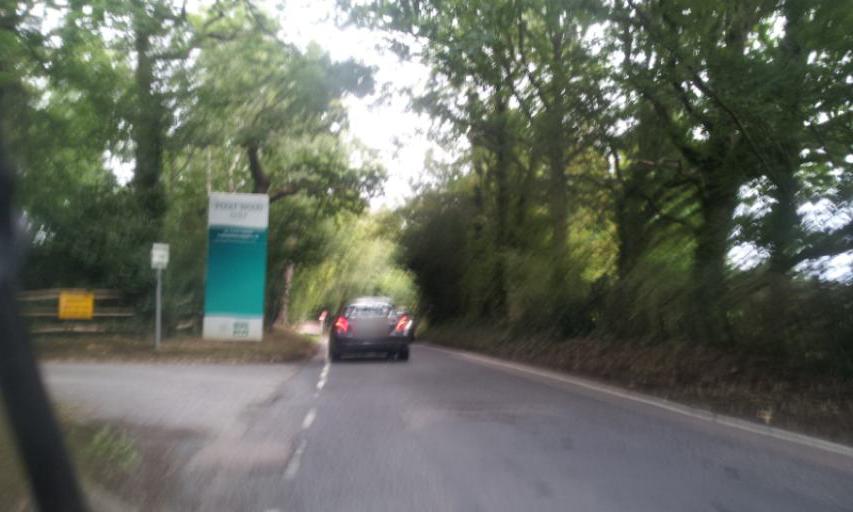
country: GB
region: England
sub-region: Kent
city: Tonbridge
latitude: 51.2273
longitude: 0.2960
